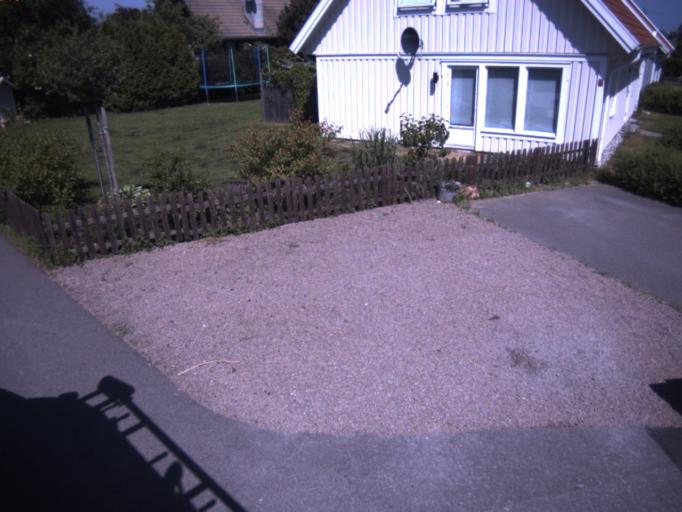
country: SE
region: Skane
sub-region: Helsingborg
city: Odakra
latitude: 56.1138
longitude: 12.6956
